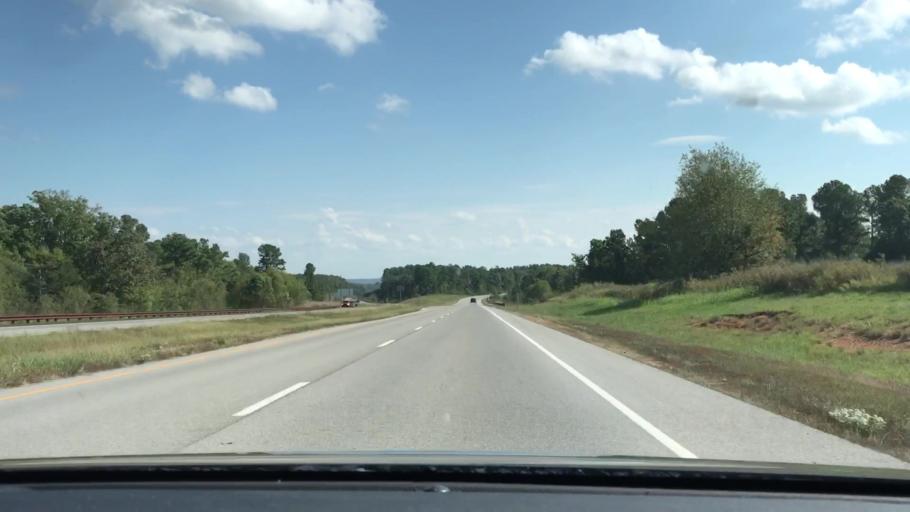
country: US
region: Kentucky
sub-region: Trigg County
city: Cadiz
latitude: 36.7808
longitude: -88.0539
